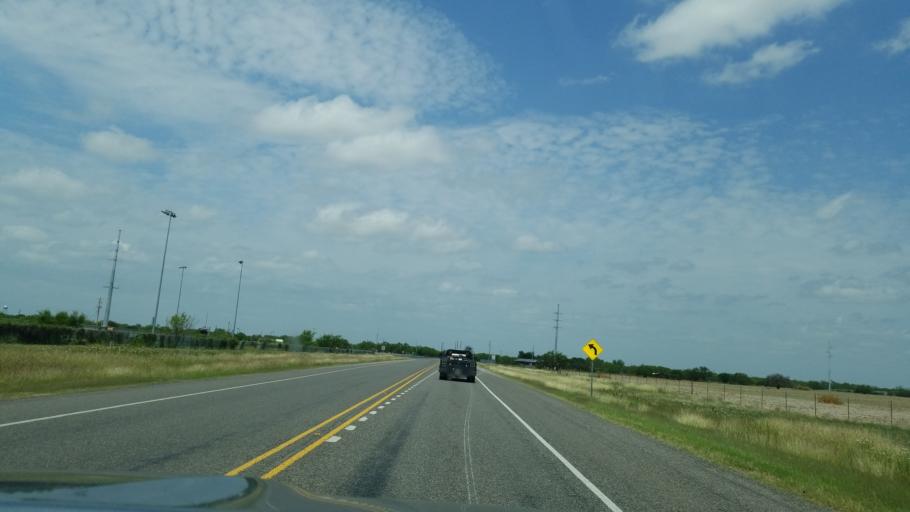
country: US
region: Texas
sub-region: Zavala County
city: La Pryor
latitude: 28.9442
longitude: -99.8308
